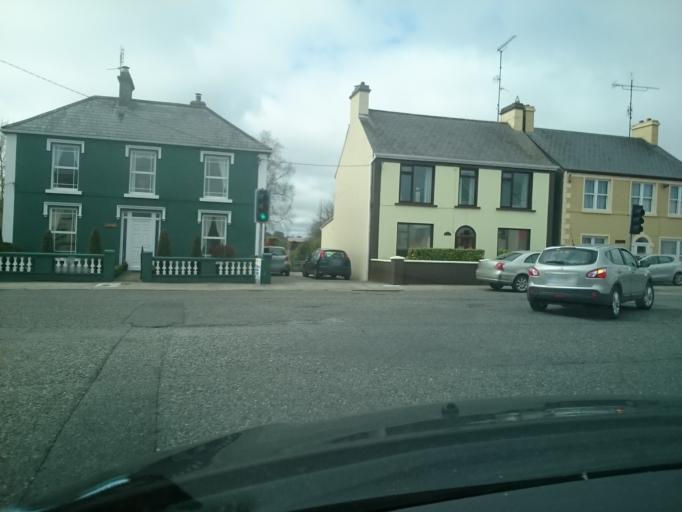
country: IE
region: Connaught
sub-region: Maigh Eo
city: Claremorris
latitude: 53.7235
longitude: -9.0012
